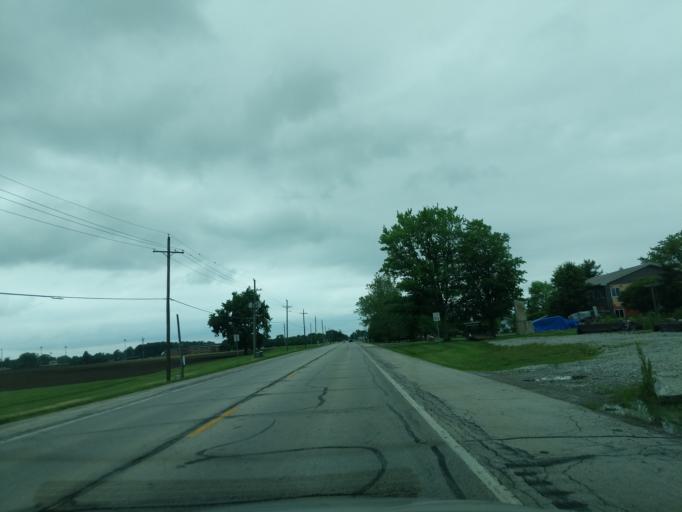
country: US
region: Indiana
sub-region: Hamilton County
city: Arcadia
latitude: 40.1586
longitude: -86.0132
